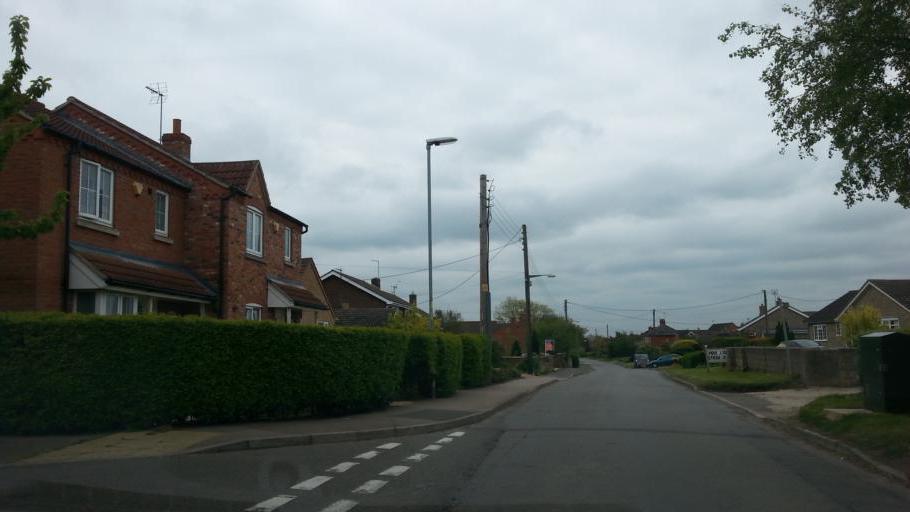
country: GB
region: England
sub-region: Lincolnshire
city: Bourne
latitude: 52.7443
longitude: -0.3757
